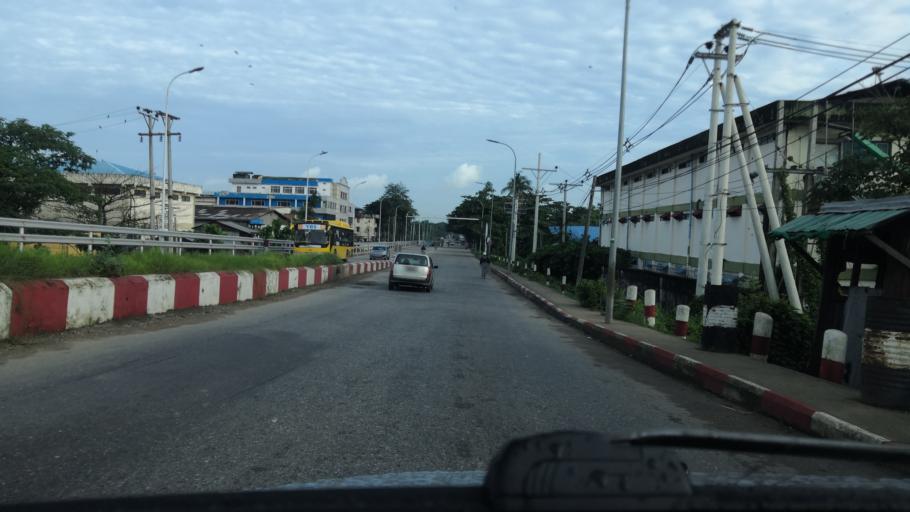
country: MM
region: Yangon
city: Yangon
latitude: 16.8901
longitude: 96.1609
